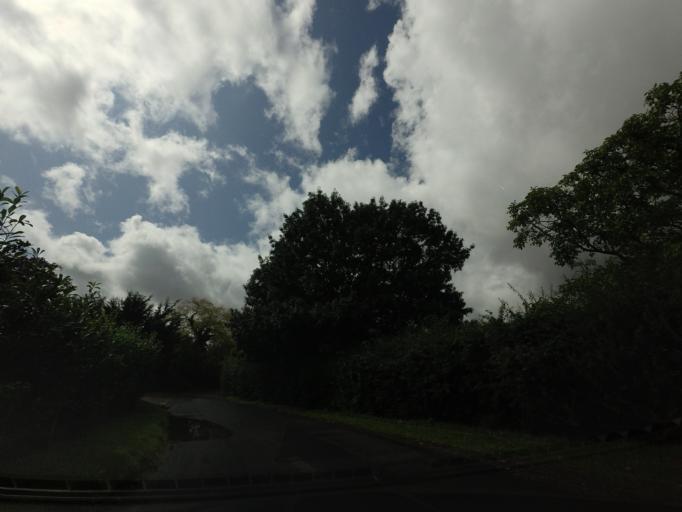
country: GB
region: England
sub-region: Kent
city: Paddock Wood
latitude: 51.1837
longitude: 0.4071
